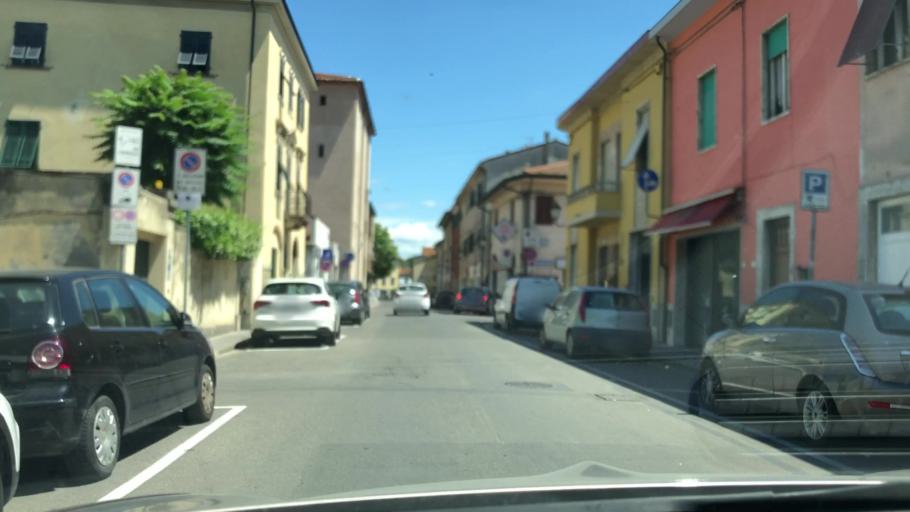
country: IT
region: Tuscany
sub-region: Province of Pisa
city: Ponsacco
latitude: 43.6199
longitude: 10.6309
